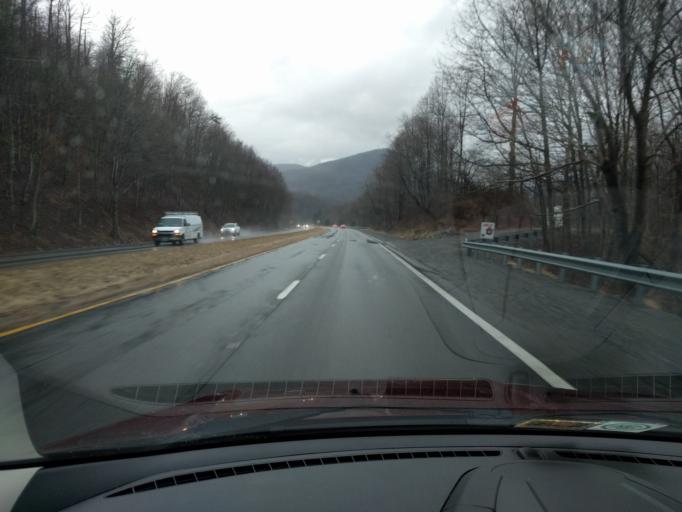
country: US
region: Virginia
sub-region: Montgomery County
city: Prices Fork
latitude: 37.2869
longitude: -80.4846
